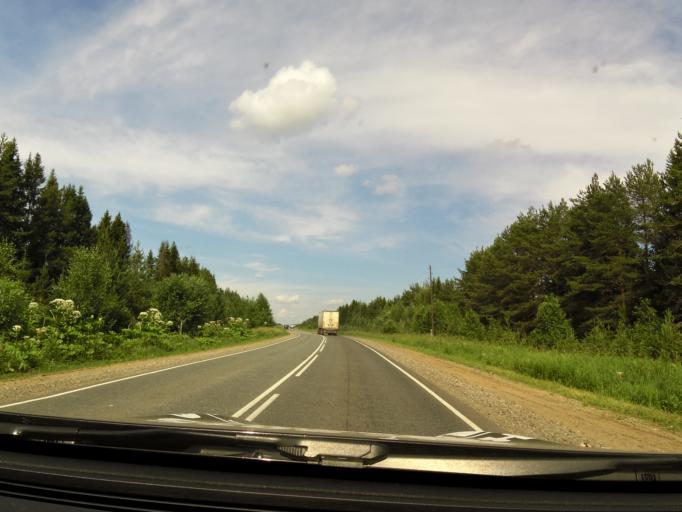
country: RU
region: Kirov
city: Slobodskoy
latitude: 58.7340
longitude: 50.2870
